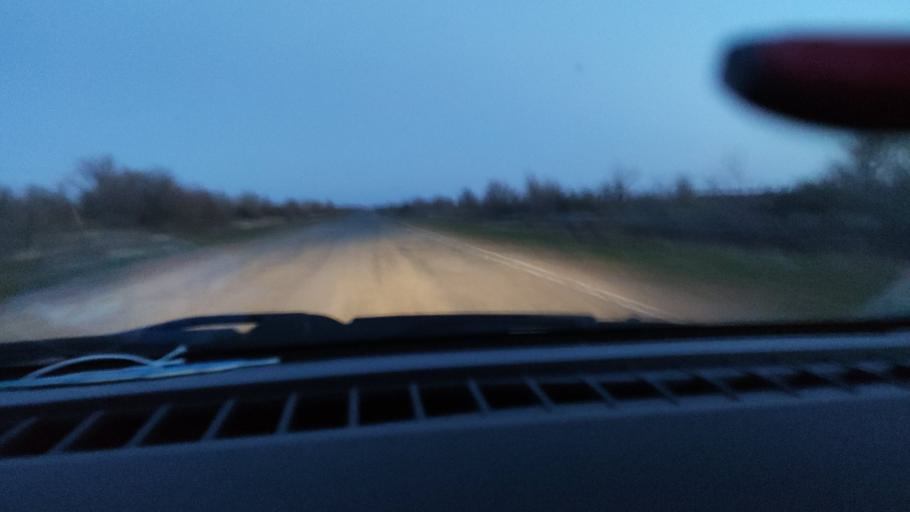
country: RU
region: Saratov
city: Rovnoye
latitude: 50.9521
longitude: 46.1227
